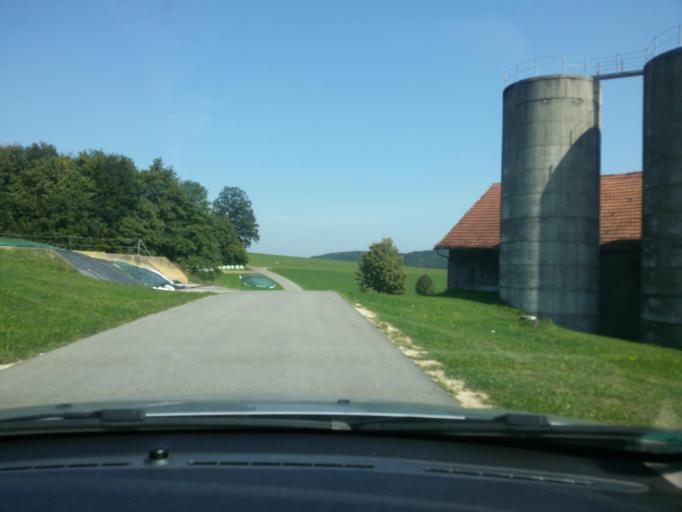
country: DE
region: Bavaria
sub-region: Swabia
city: Scherstetten
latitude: 48.2037
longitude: 10.6182
